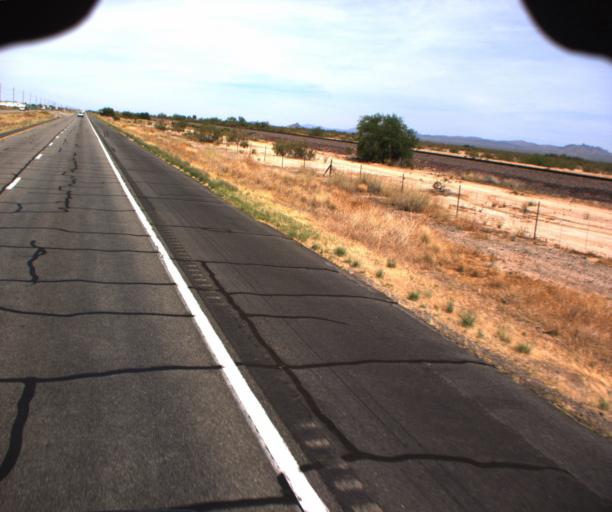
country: US
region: Arizona
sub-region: Maricopa County
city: Sun City West
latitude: 33.7595
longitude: -112.5049
